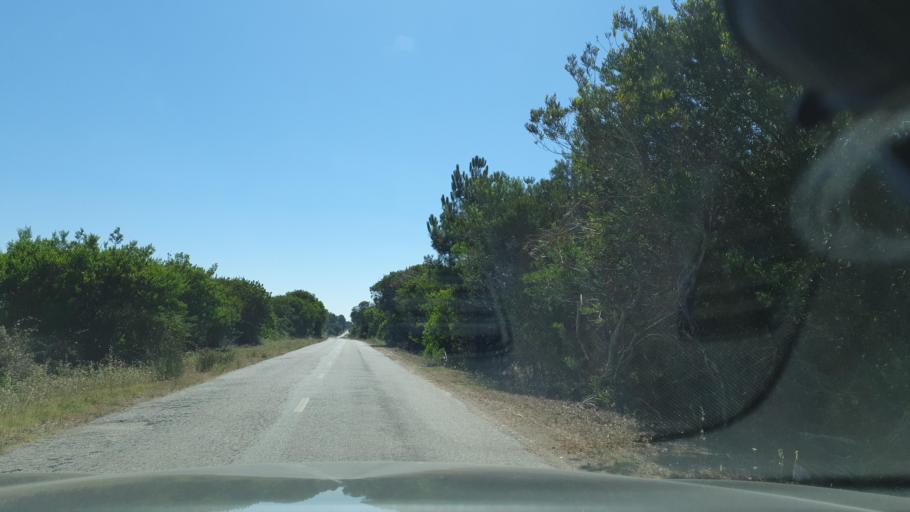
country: PT
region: Beja
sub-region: Odemira
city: Sao Teotonio
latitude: 37.5002
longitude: -8.6785
